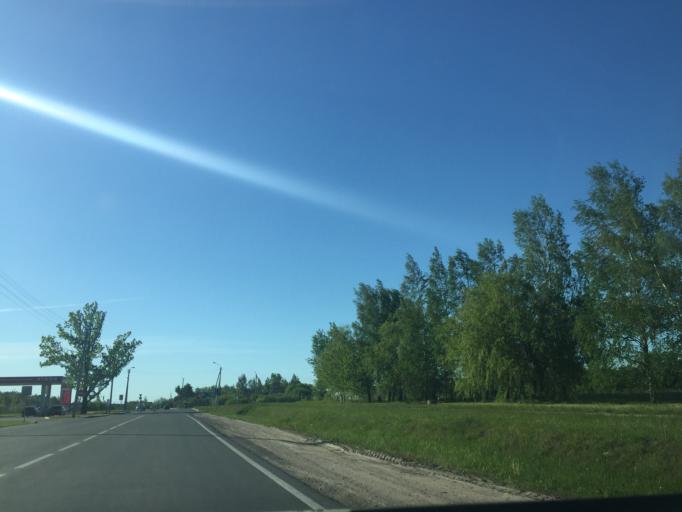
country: LT
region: Panevezys
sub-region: Panevezys City
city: Panevezys
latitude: 55.7527
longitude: 24.3134
